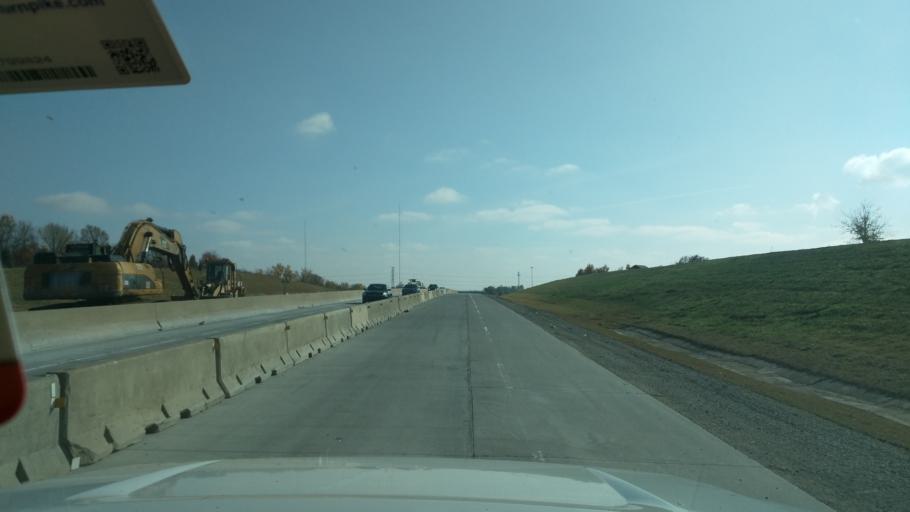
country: US
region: Oklahoma
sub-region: Tulsa County
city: Broken Arrow
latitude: 36.0378
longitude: -95.7183
